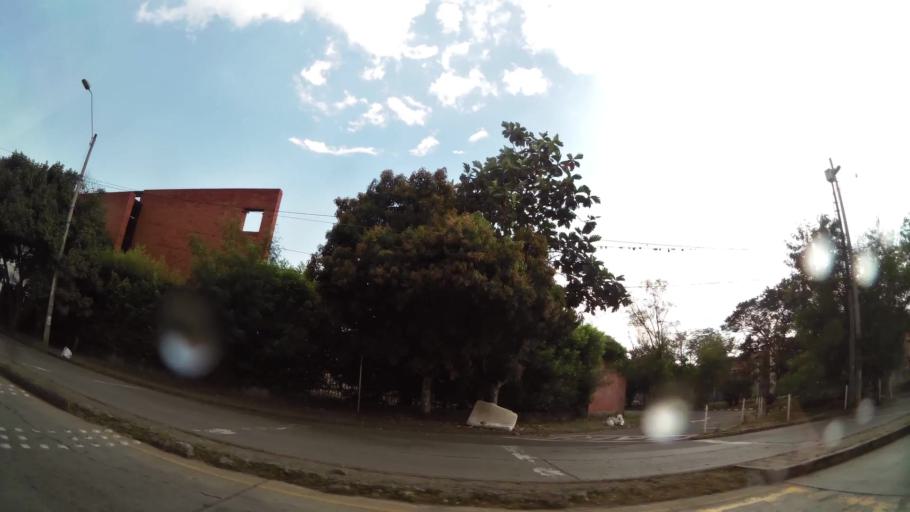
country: CO
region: Valle del Cauca
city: Cali
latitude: 3.4659
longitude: -76.4905
